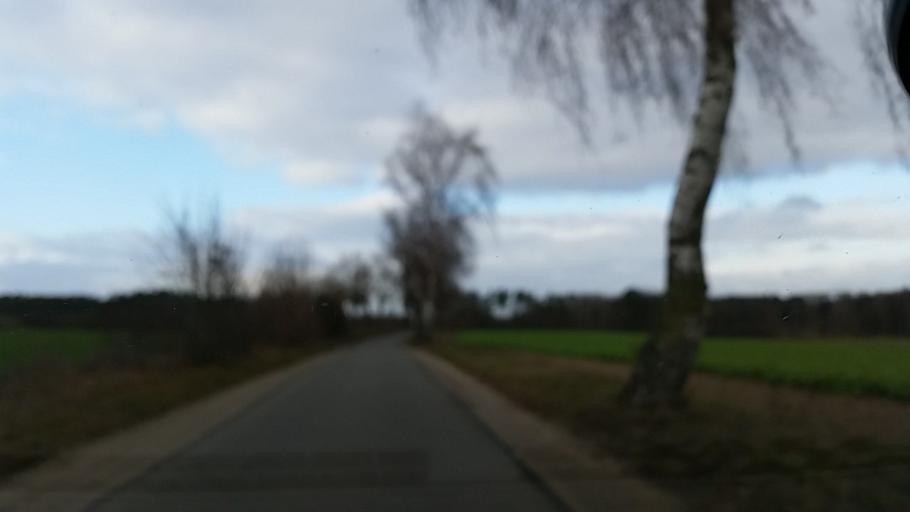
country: DE
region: Lower Saxony
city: Wieren
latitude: 52.8667
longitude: 10.6634
